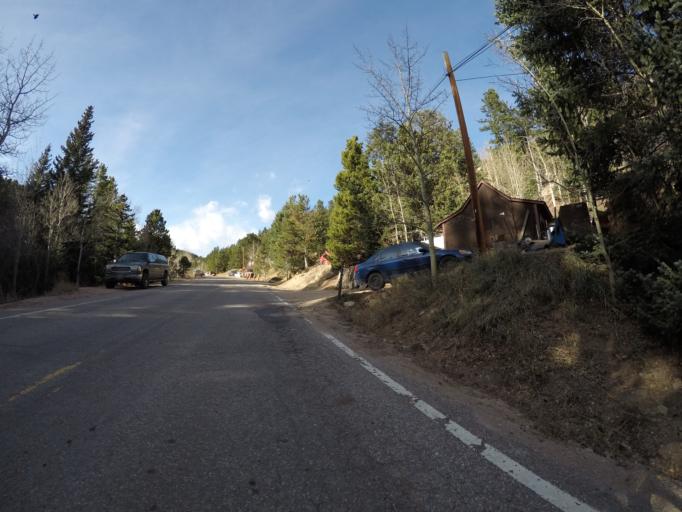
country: US
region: Colorado
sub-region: Boulder County
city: Nederland
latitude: 40.0695
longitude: -105.5049
